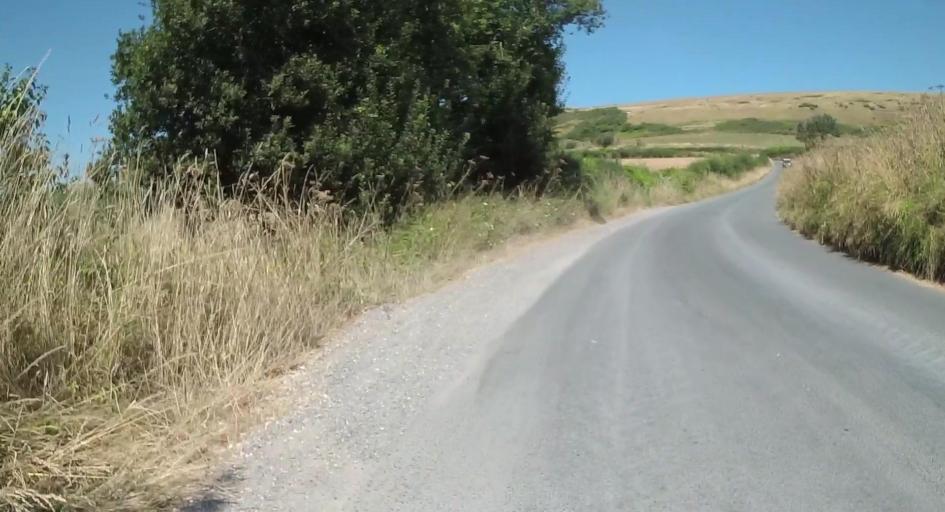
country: GB
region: England
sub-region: Dorset
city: Wareham
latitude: 50.6303
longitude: -2.1324
